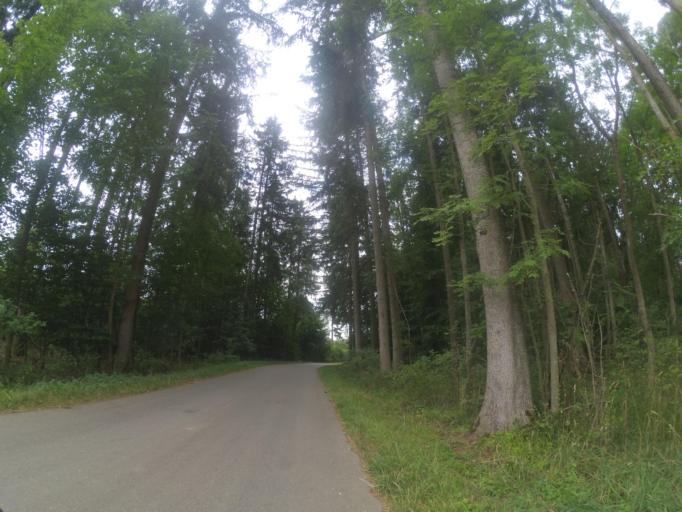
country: DE
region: Baden-Wuerttemberg
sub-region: Tuebingen Region
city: Westerstetten
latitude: 48.5132
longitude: 9.9387
